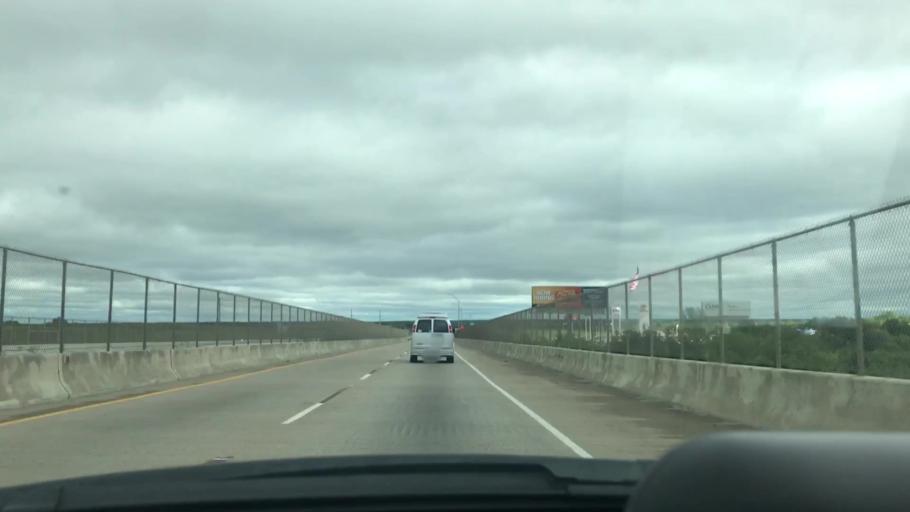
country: US
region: Texas
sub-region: Grayson County
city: Denison
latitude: 33.7710
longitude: -96.5848
